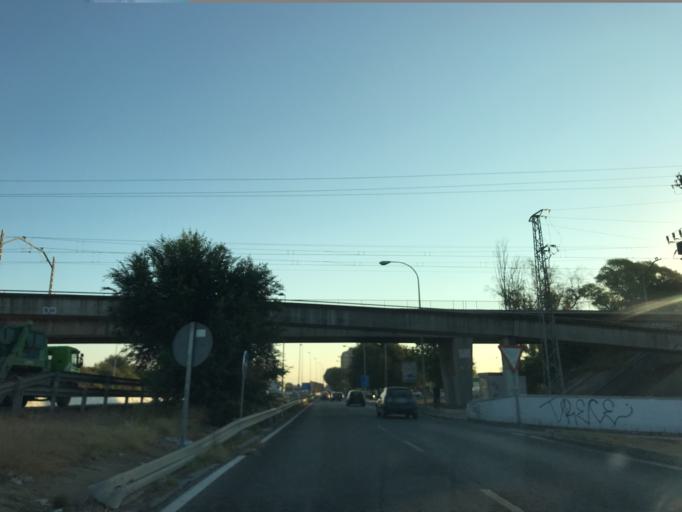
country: ES
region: Andalusia
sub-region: Provincia de Sevilla
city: Sevilla
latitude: 37.4098
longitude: -5.9406
